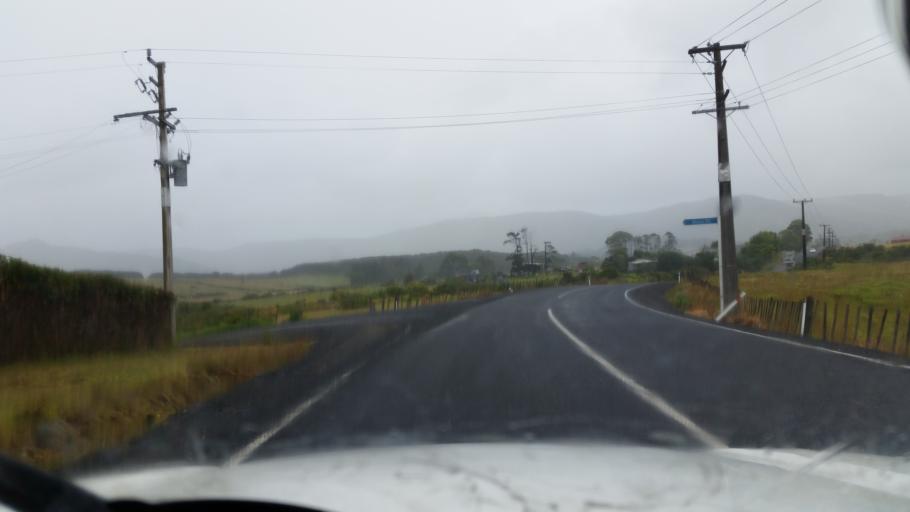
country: NZ
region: Northland
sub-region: Far North District
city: Ahipara
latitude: -35.1749
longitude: 173.1780
